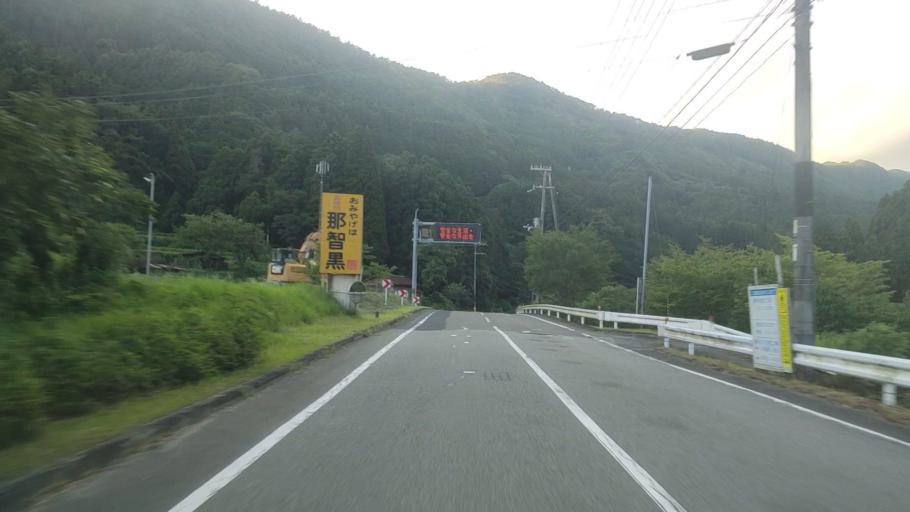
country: JP
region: Wakayama
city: Tanabe
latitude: 33.8236
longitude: 135.6313
